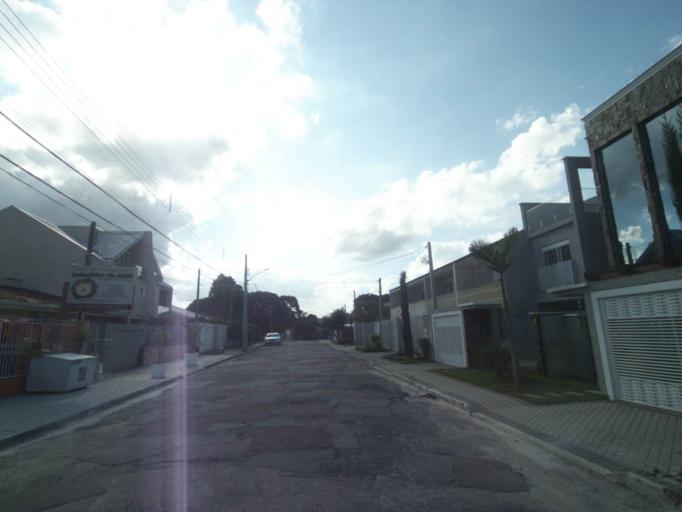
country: BR
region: Parana
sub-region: Pinhais
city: Pinhais
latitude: -25.4375
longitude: -49.2203
